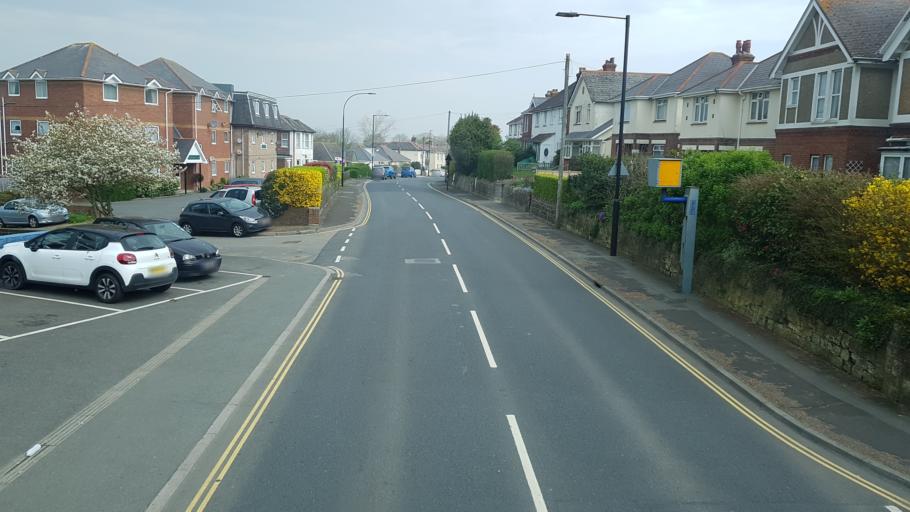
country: GB
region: England
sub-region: Isle of Wight
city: Shanklin
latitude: 50.6384
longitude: -1.1721
